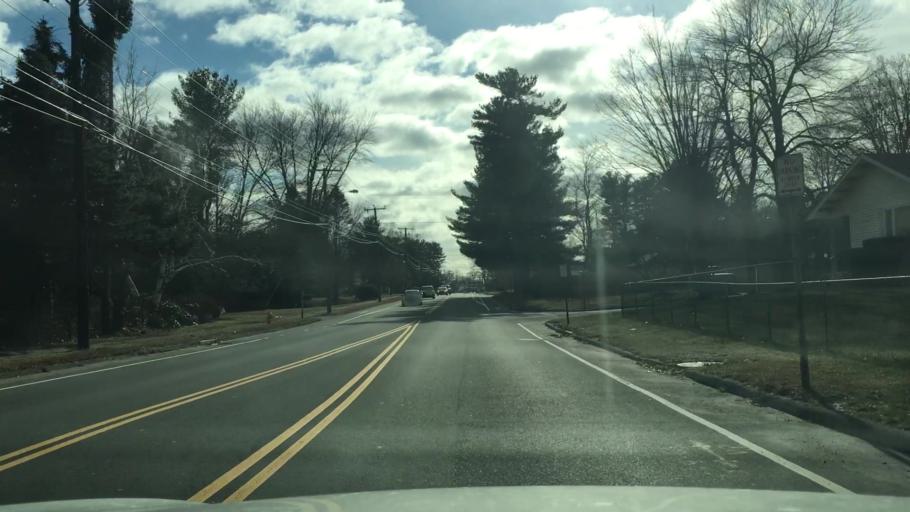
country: US
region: Massachusetts
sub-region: Hampden County
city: Agawam
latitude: 42.0667
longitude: -72.6316
